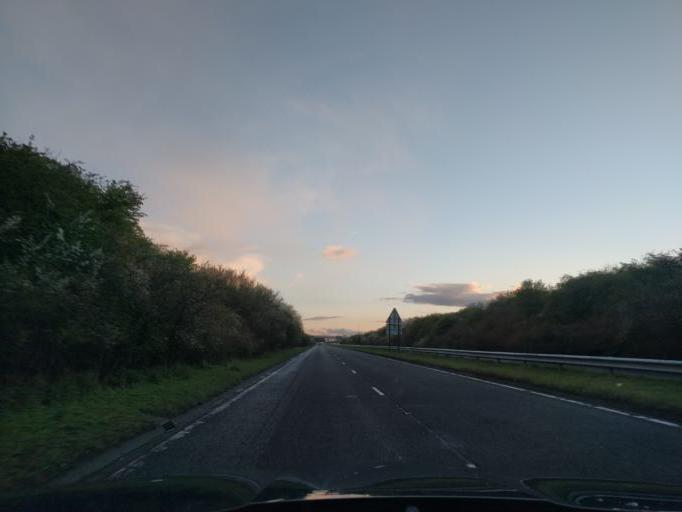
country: GB
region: England
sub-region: Northumberland
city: Seghill
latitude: 55.0510
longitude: -1.5815
